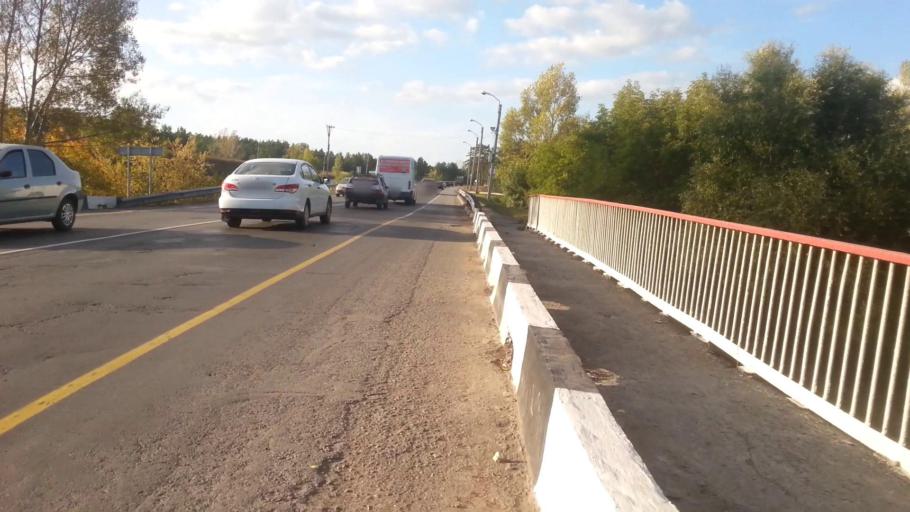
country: RU
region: Altai Krai
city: Yuzhnyy
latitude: 53.3064
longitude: 83.7029
